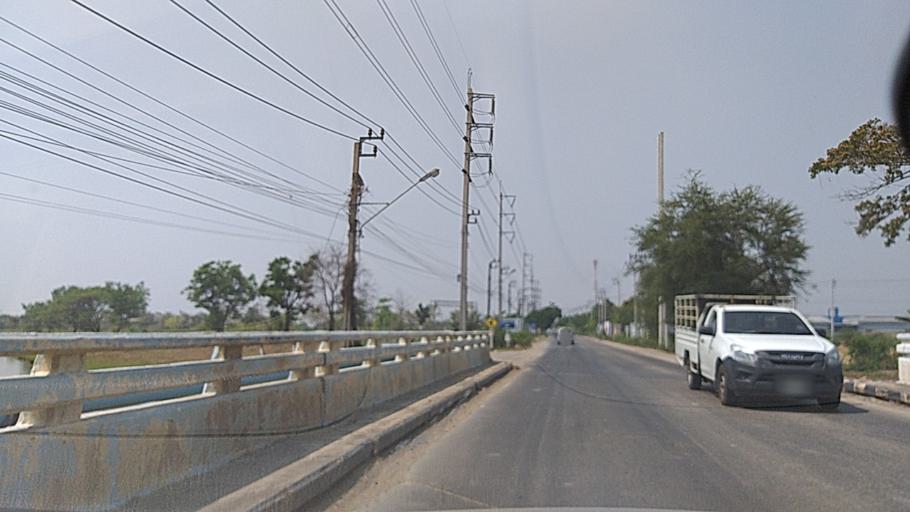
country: TH
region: Nonthaburi
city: Sai Noi
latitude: 13.9384
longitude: 100.3163
